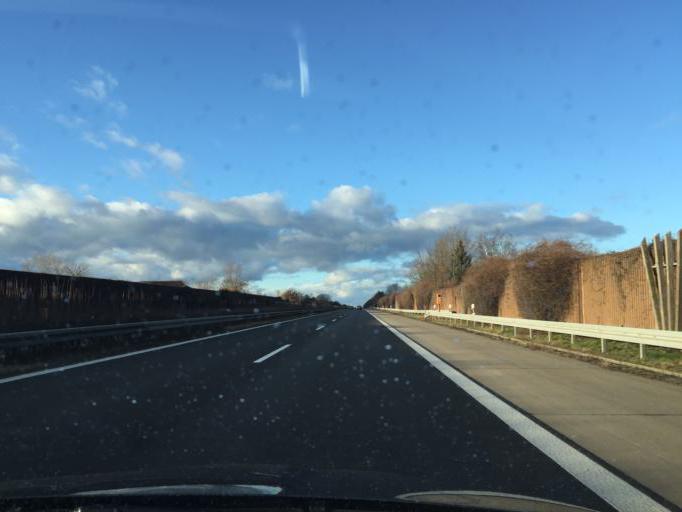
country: DE
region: Brandenburg
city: Vetschau
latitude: 51.7983
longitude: 14.0481
